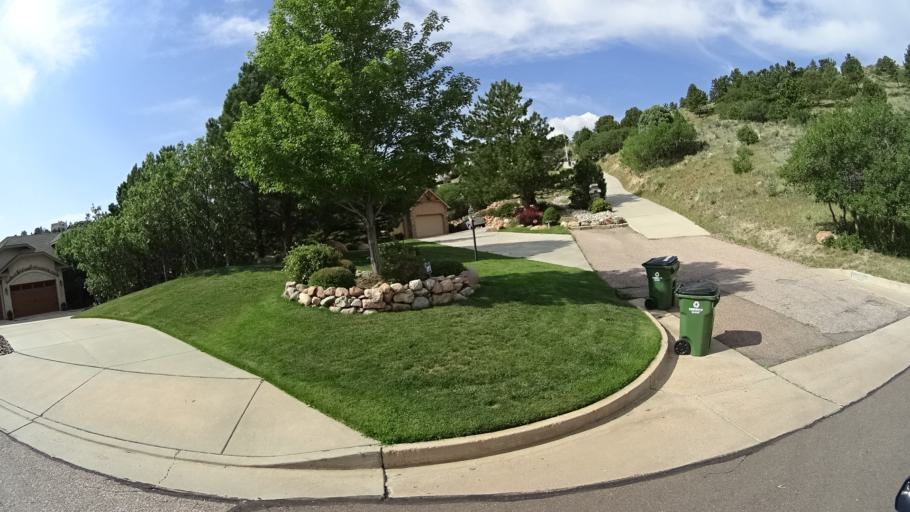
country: US
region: Colorado
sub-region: El Paso County
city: Air Force Academy
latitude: 38.9419
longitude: -104.8698
